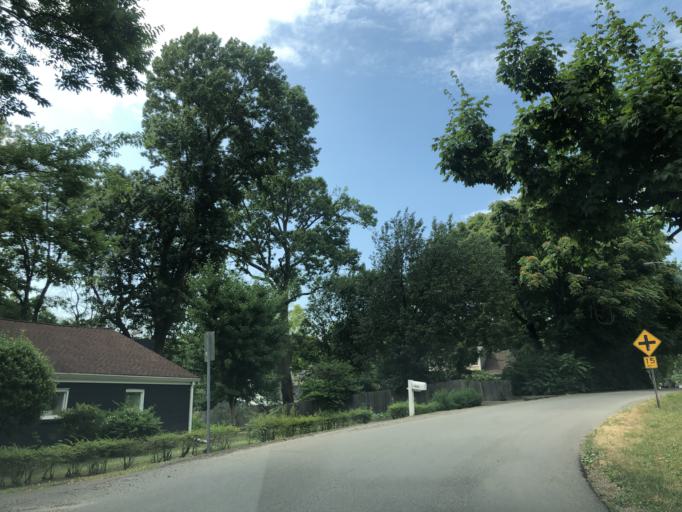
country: US
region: Tennessee
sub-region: Davidson County
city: Oak Hill
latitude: 36.1220
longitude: -86.8025
